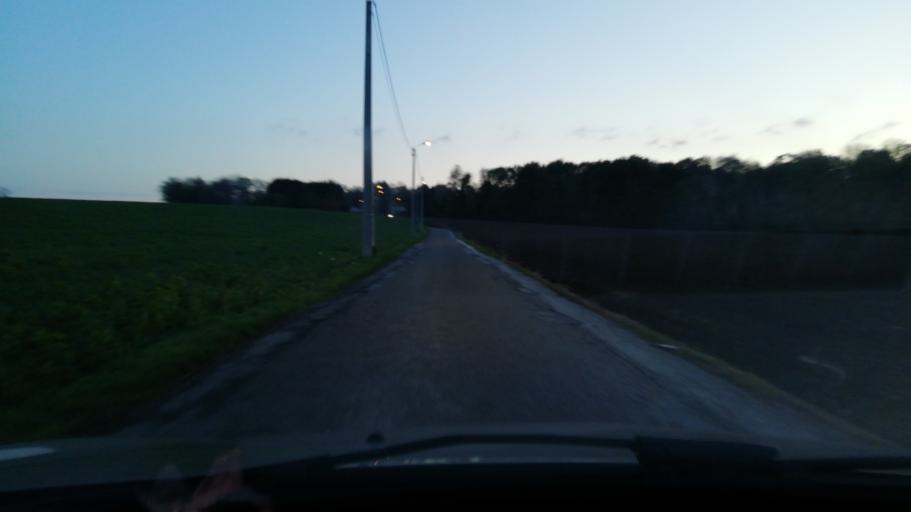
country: FR
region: Nord-Pas-de-Calais
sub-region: Departement du Nord
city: Marpent
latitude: 50.2814
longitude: 4.0898
